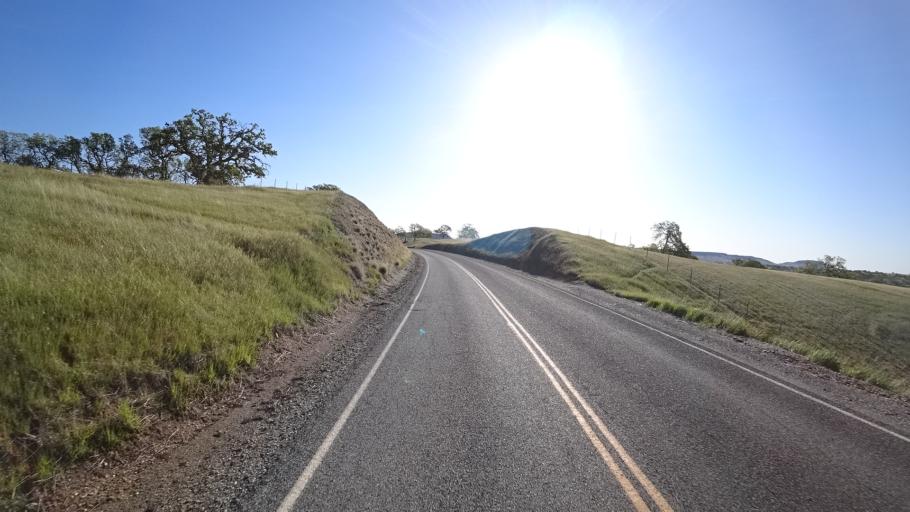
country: US
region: California
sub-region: Tehama County
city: Rancho Tehama Reserve
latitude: 39.8118
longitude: -122.3950
